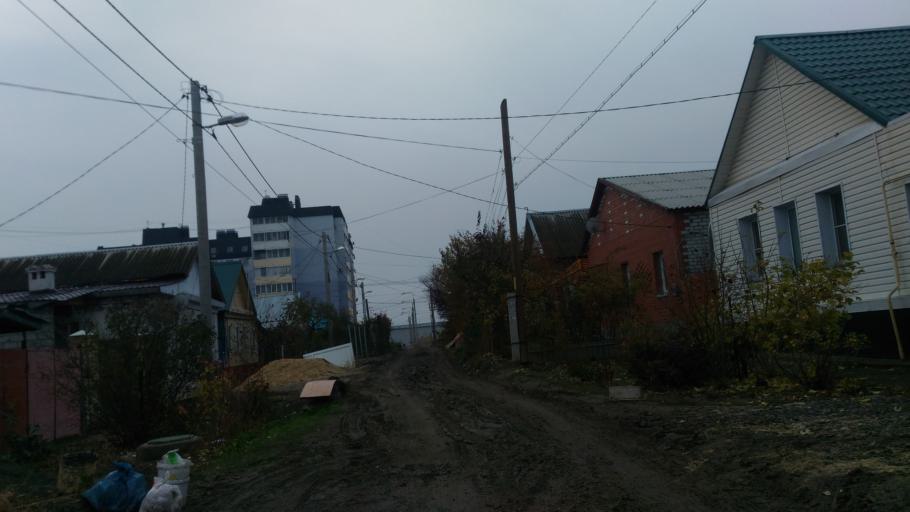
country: RU
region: Volgograd
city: Volgograd
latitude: 48.6466
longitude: 44.4298
